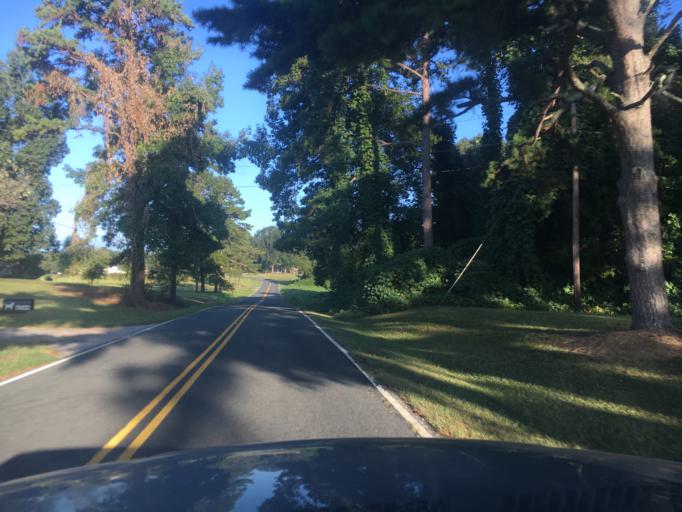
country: US
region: South Carolina
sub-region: Spartanburg County
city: Woodruff
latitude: 34.6375
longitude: -82.0138
